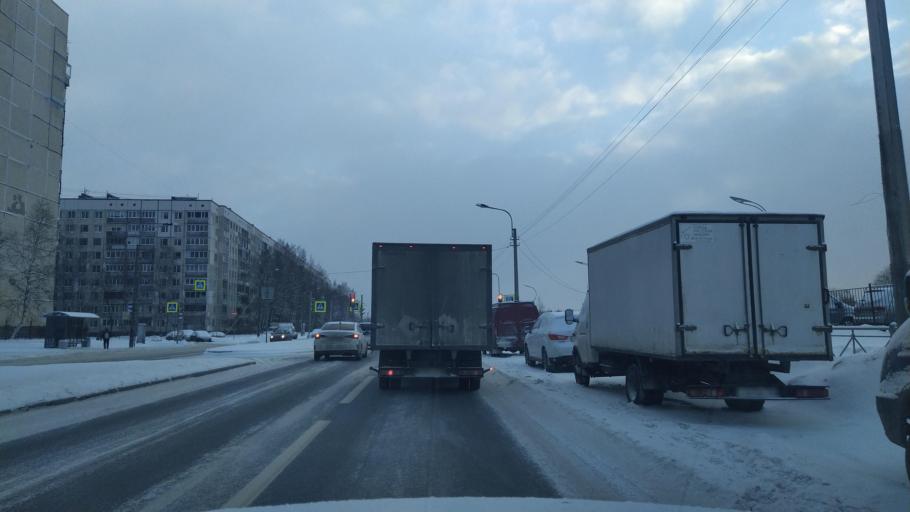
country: RU
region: St.-Petersburg
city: Grazhdanka
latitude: 60.0237
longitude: 30.4175
